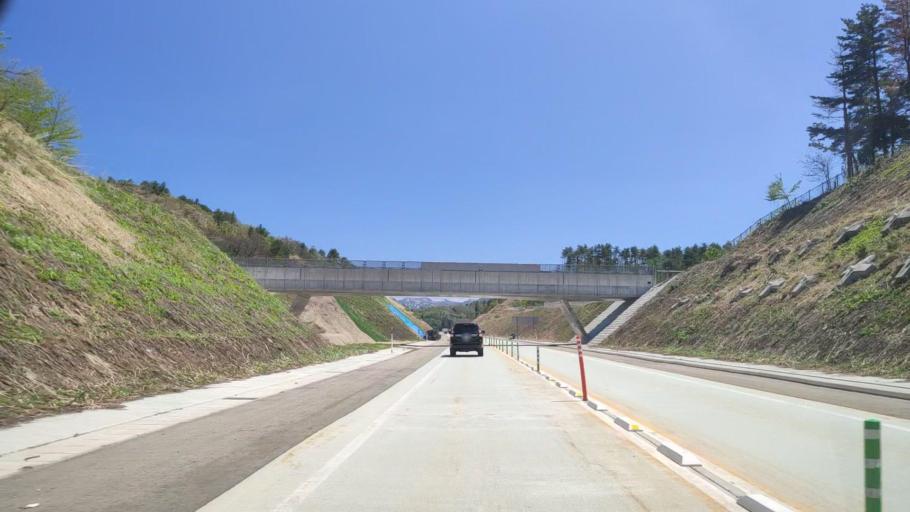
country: JP
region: Yamagata
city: Obanazawa
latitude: 38.5879
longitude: 140.3910
